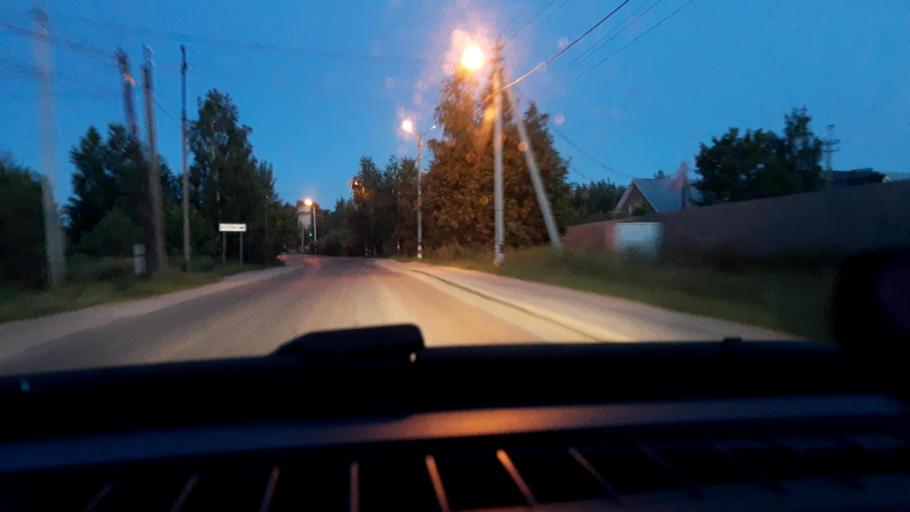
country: RU
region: Nizjnij Novgorod
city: Bor
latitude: 56.3835
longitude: 44.0385
